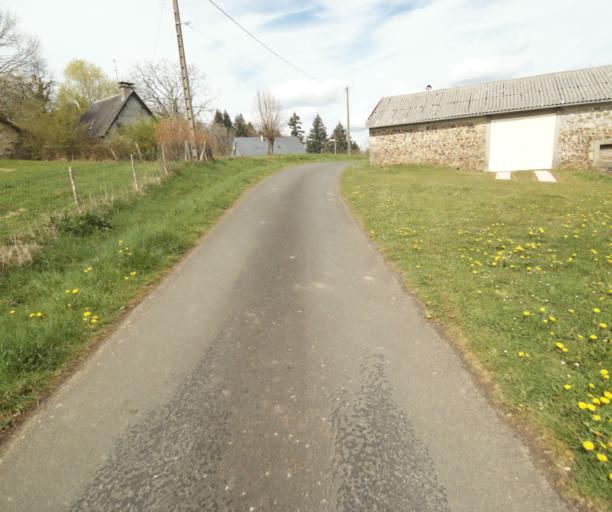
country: FR
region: Limousin
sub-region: Departement de la Correze
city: Sainte-Fortunade
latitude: 45.2033
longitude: 1.8424
